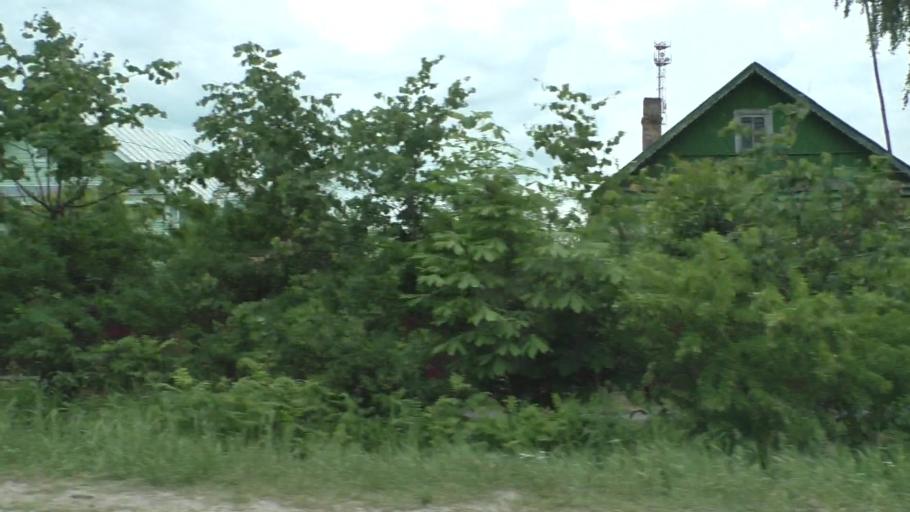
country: RU
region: Moskovskaya
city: Il'inskiy Pogost
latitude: 55.5037
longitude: 38.7844
